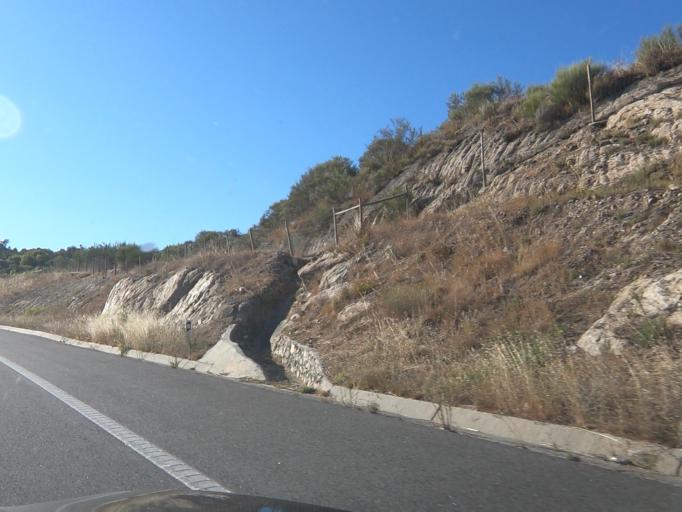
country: PT
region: Vila Real
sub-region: Murca
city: Murca
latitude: 41.3894
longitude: -7.4719
